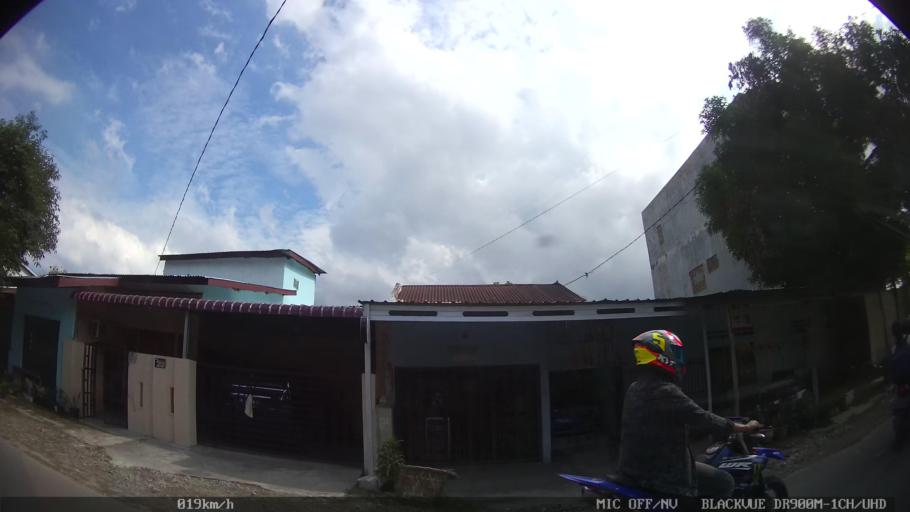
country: ID
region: North Sumatra
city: Medan
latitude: 3.6207
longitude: 98.6661
